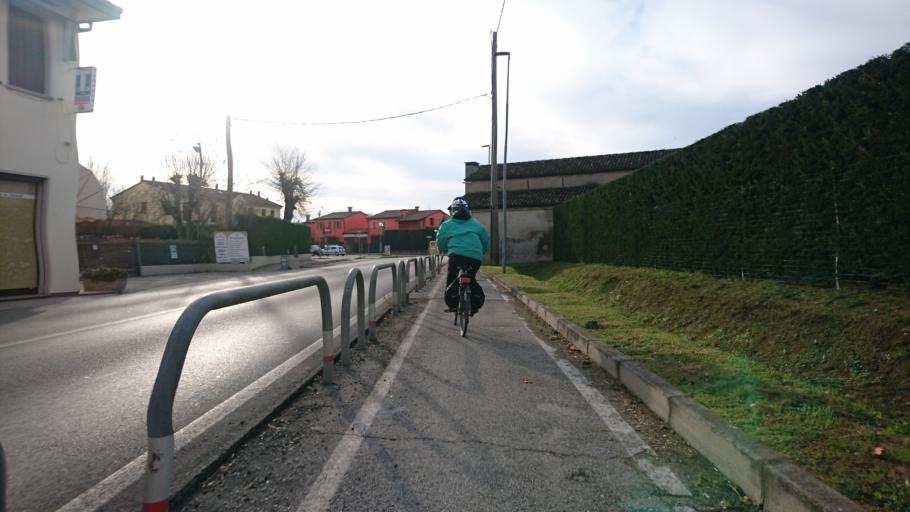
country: IT
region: Veneto
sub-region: Provincia di Padova
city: Polverara
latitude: 45.3186
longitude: 11.9632
